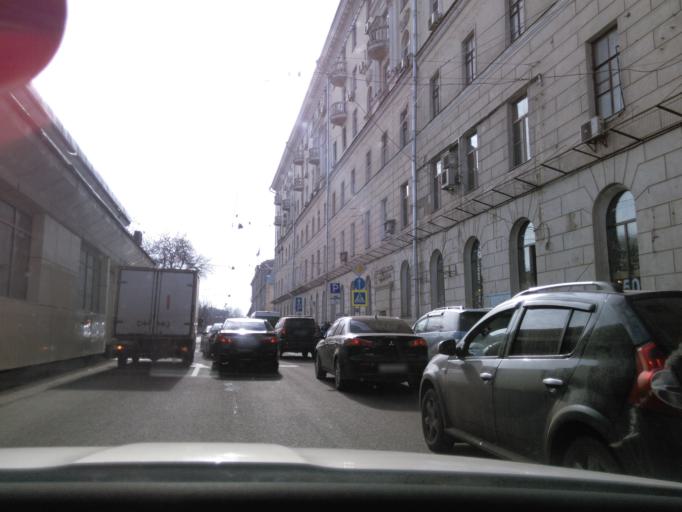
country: RU
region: Moscow
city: Moscow
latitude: 55.7648
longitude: 37.6381
